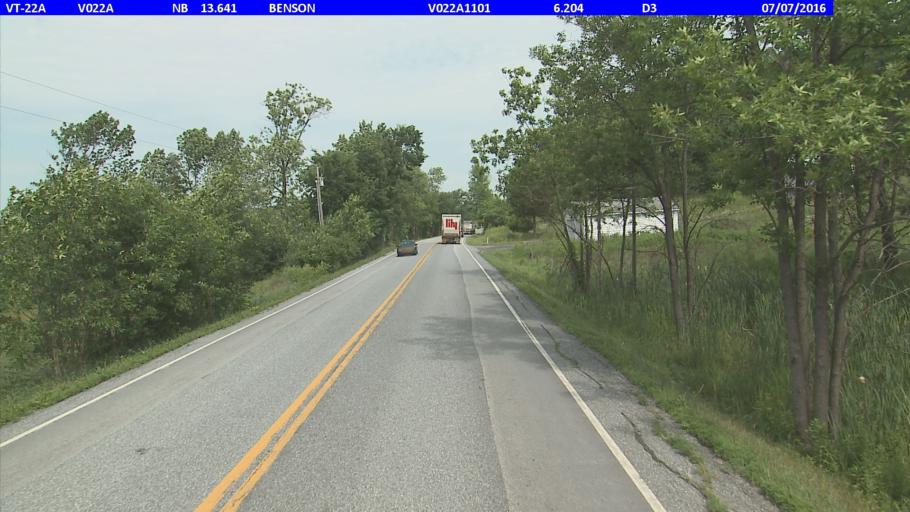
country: US
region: New York
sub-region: Essex County
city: Ticonderoga
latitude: 43.7565
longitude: -73.3106
